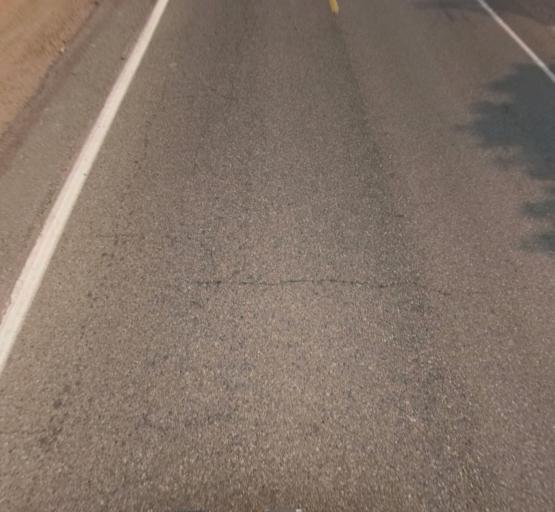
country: US
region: California
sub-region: Madera County
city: Madera Acres
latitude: 37.0489
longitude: -120.0564
